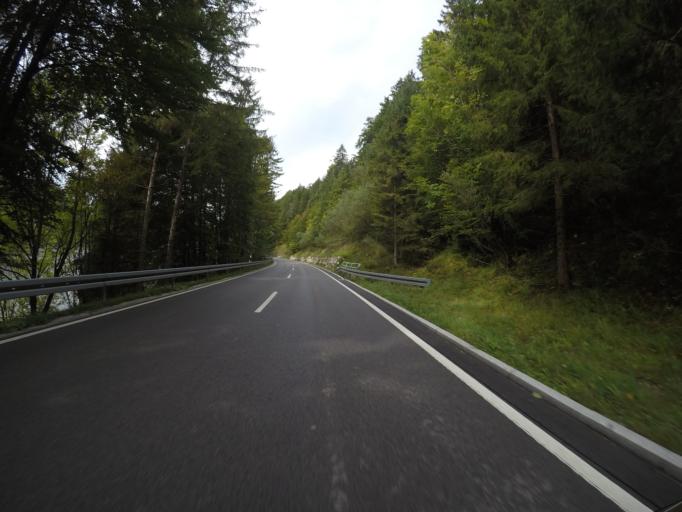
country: DE
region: Bavaria
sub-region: Upper Bavaria
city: Lenggries
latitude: 47.5850
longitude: 11.5766
